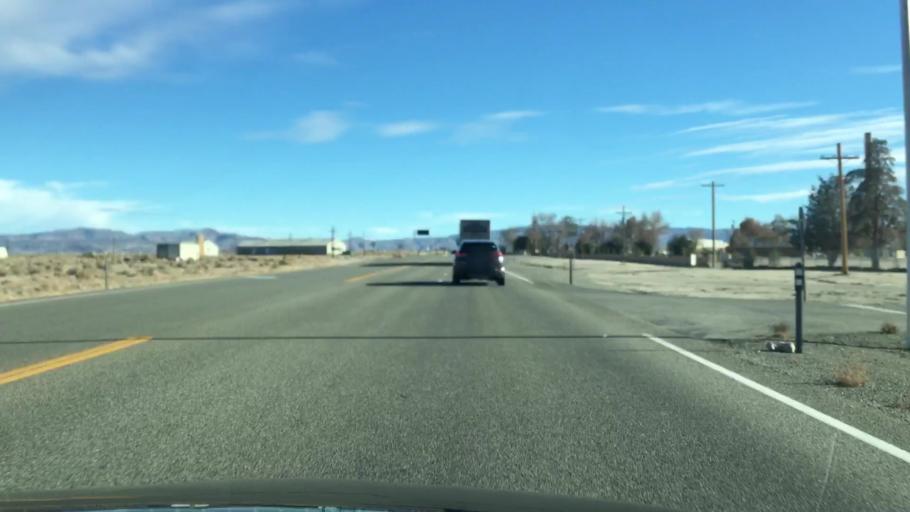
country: US
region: Nevada
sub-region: Mineral County
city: Hawthorne
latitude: 38.5498
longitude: -118.6550
